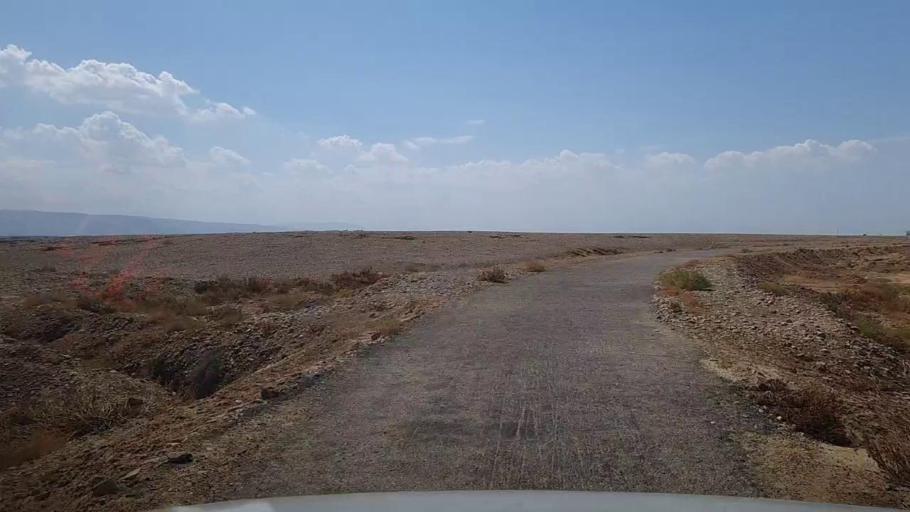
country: PK
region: Sindh
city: Bhan
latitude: 26.3815
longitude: 67.6296
